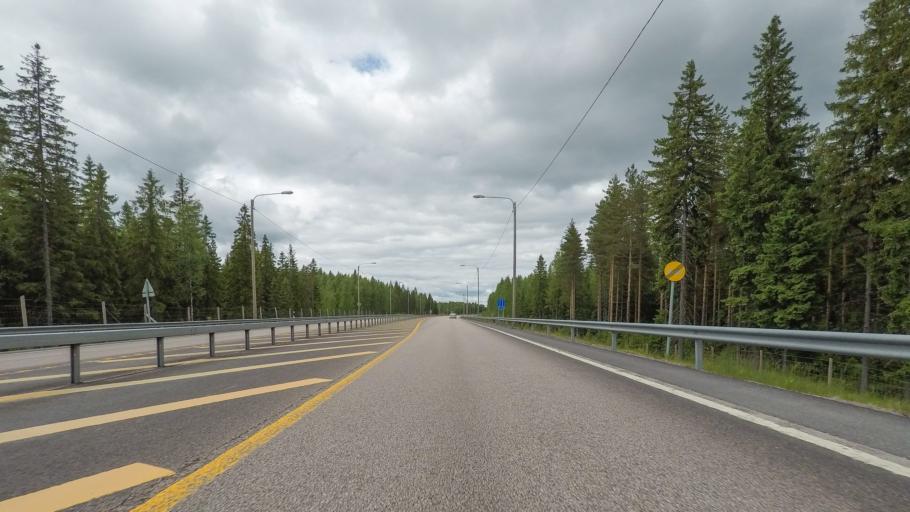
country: FI
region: Paijanne Tavastia
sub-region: Lahti
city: Hartola
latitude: 61.4557
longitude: 25.9836
